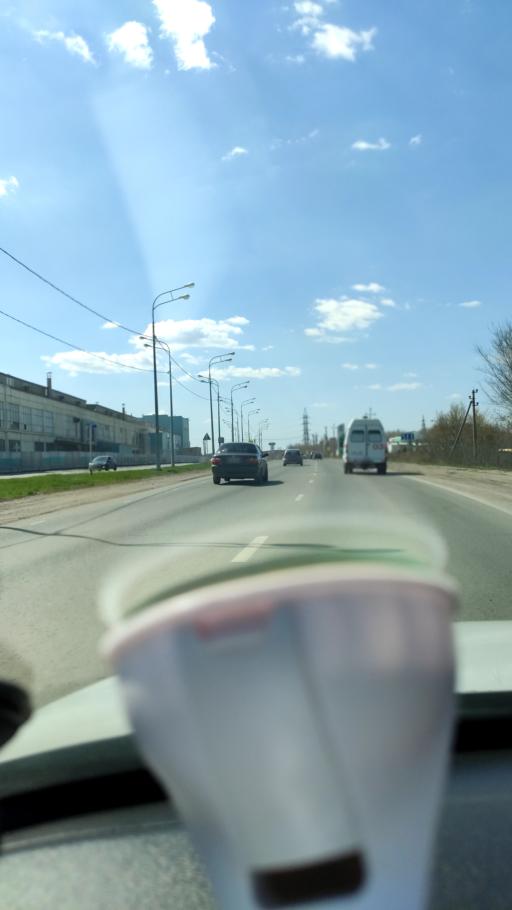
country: RU
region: Samara
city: Smyshlyayevka
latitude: 53.2674
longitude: 50.3953
